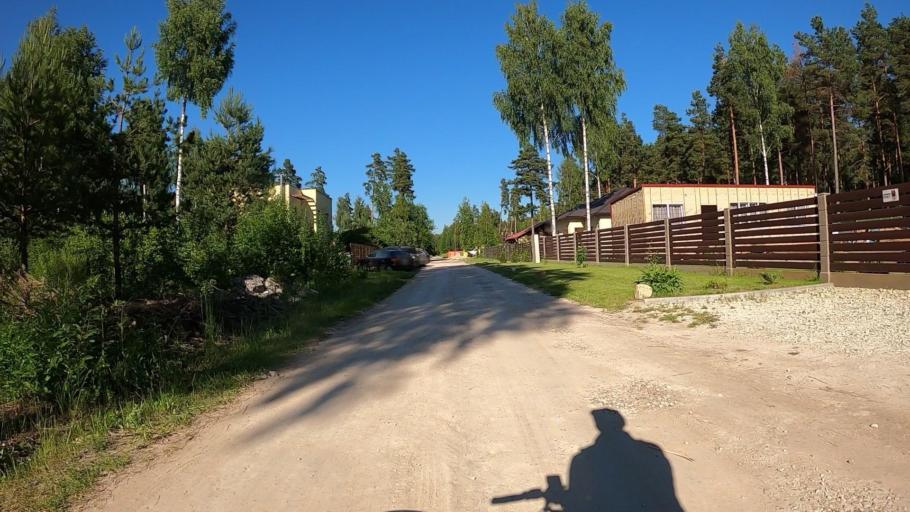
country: LV
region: Stopini
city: Ulbroka
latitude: 56.8768
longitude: 24.2921
